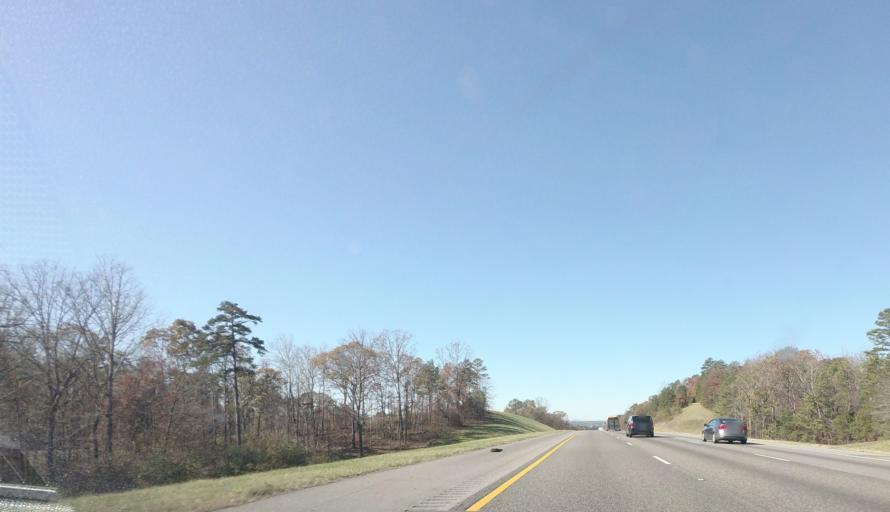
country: US
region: Alabama
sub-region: Calhoun County
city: Bynum
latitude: 33.5761
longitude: -85.9951
